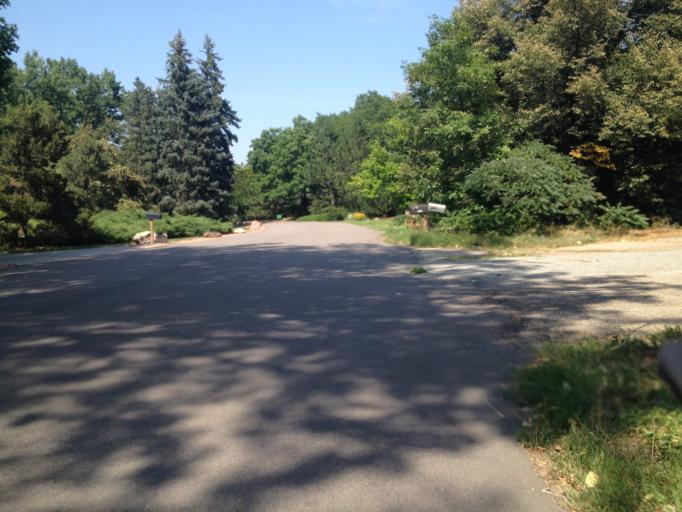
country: US
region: Colorado
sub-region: Boulder County
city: Boulder
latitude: 40.0113
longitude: -105.2160
